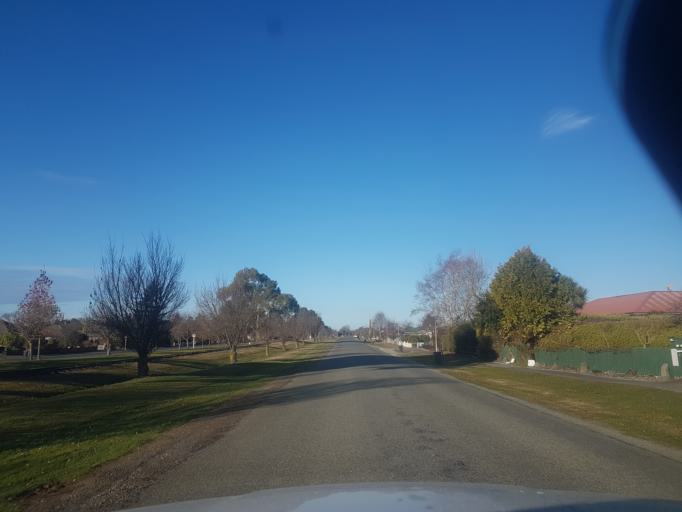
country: NZ
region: Canterbury
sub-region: Timaru District
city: Pleasant Point
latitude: -44.2618
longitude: 171.1328
